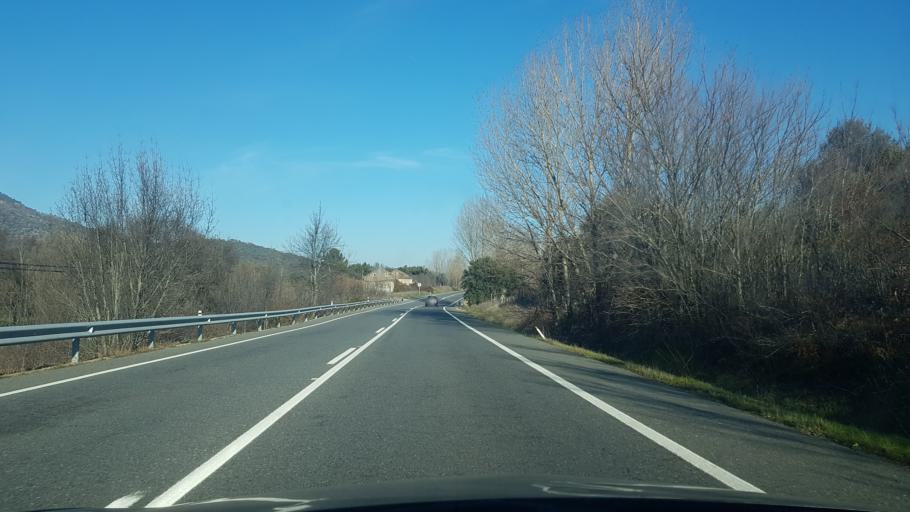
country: ES
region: Madrid
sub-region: Provincia de Madrid
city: Rozas de Puerto Real
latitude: 40.3299
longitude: -4.4727
